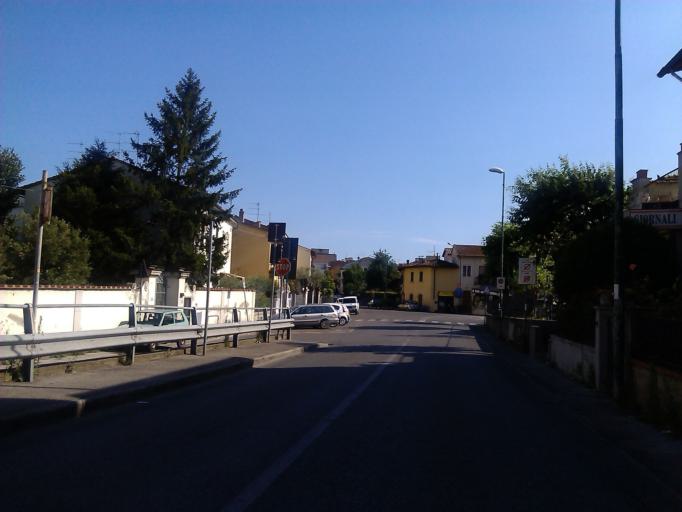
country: IT
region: Tuscany
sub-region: Province of Florence
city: Campi Bisenzio
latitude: 43.8382
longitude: 11.1321
